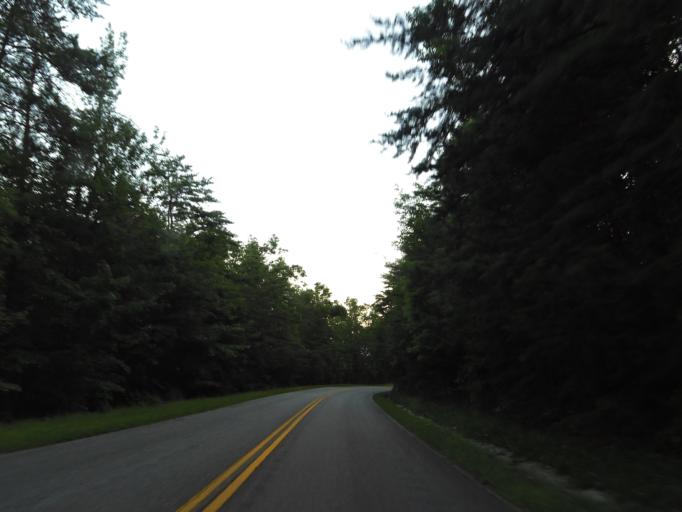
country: US
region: Tennessee
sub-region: Blount County
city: Maryville
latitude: 35.6074
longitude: -83.9788
